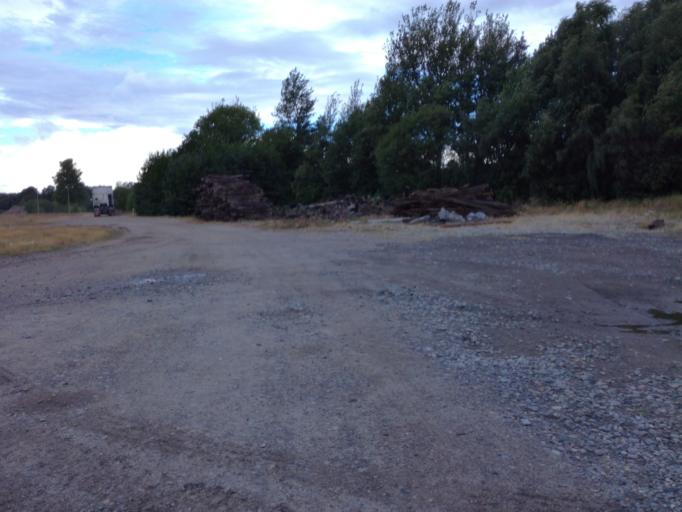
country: DK
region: South Denmark
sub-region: Fredericia Kommune
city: Fredericia
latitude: 55.5626
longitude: 9.7418
